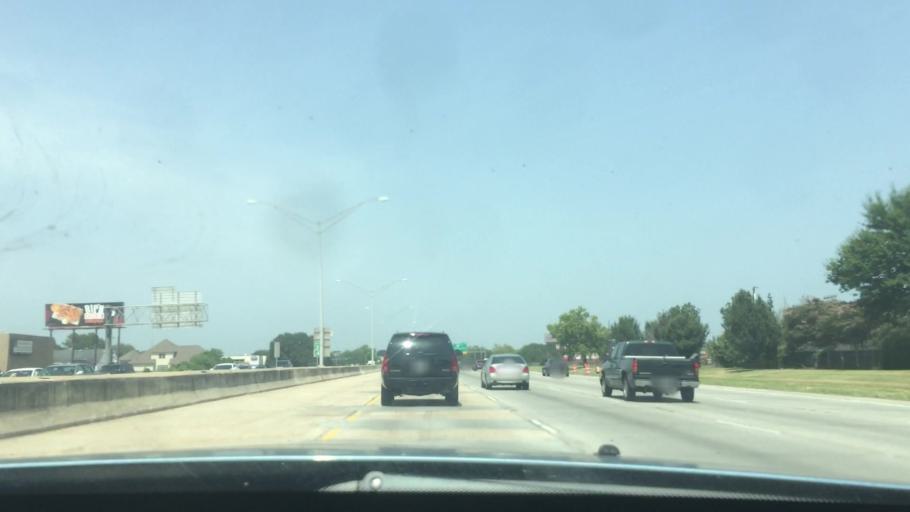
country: US
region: Louisiana
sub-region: East Baton Rouge Parish
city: Westminster
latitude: 30.4206
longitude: -91.0824
